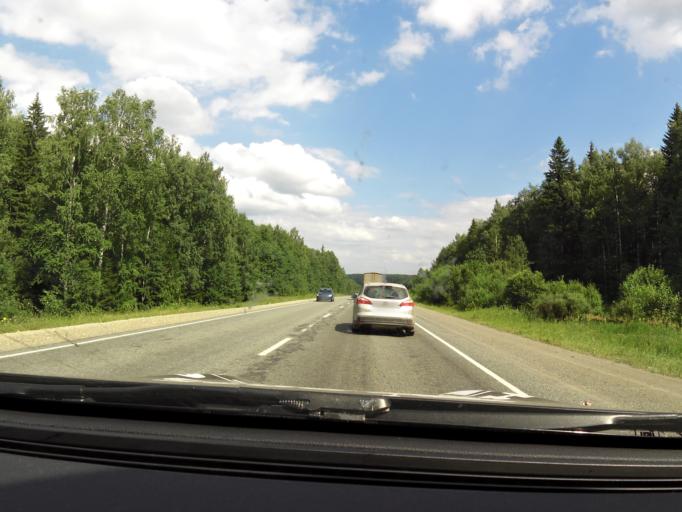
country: RU
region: Sverdlovsk
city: Bisert'
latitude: 56.8294
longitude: 59.0877
